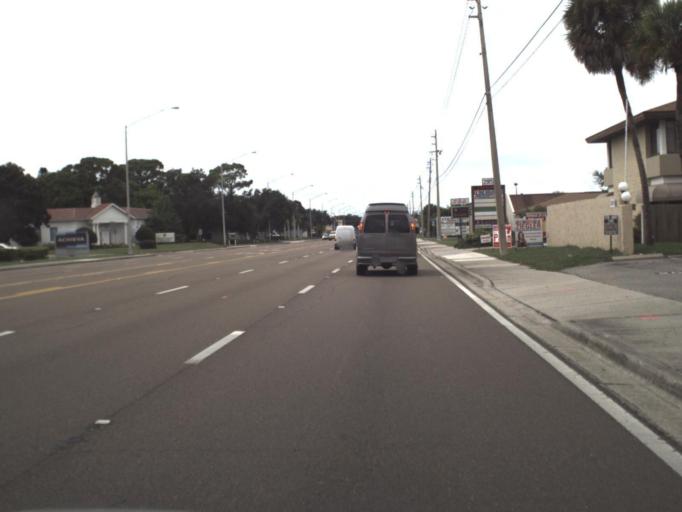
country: US
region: Florida
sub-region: Sarasota County
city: Southgate
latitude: 27.2989
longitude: -82.5090
